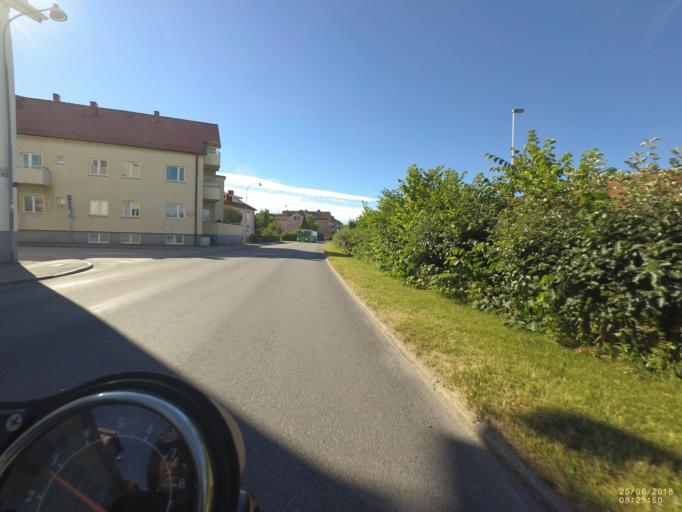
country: SE
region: Soedermanland
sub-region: Nykopings Kommun
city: Nykoping
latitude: 58.7543
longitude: 16.9967
